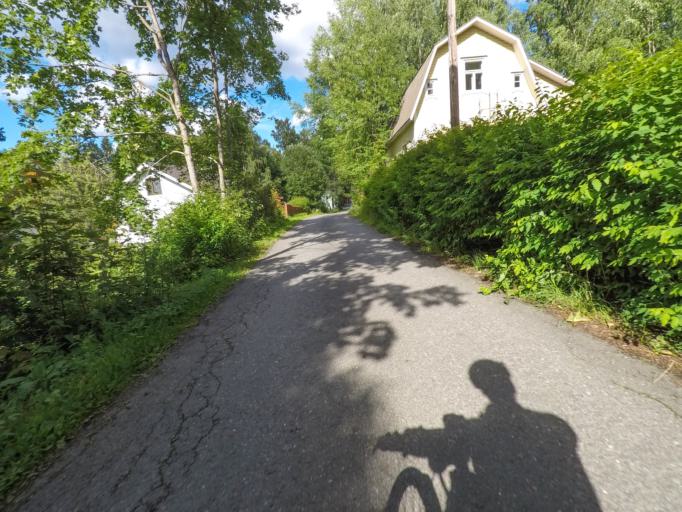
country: FI
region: South Karelia
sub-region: Lappeenranta
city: Joutseno
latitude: 61.1242
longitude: 28.4873
